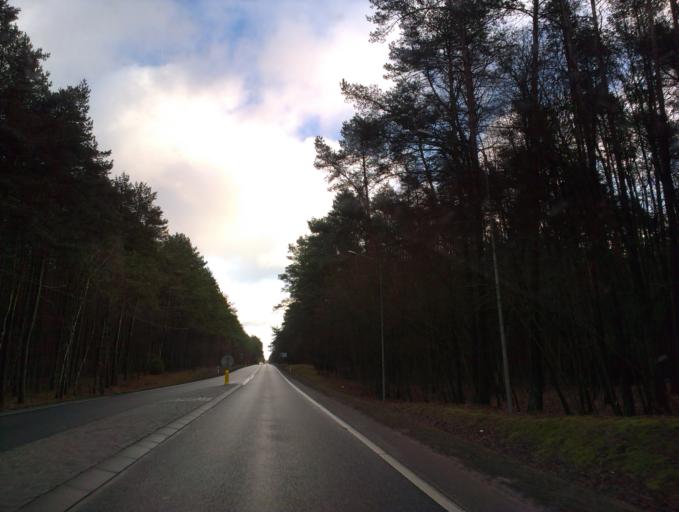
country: PL
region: Pomeranian Voivodeship
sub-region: Powiat czluchowski
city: Czluchow
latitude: 53.6422
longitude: 17.2902
